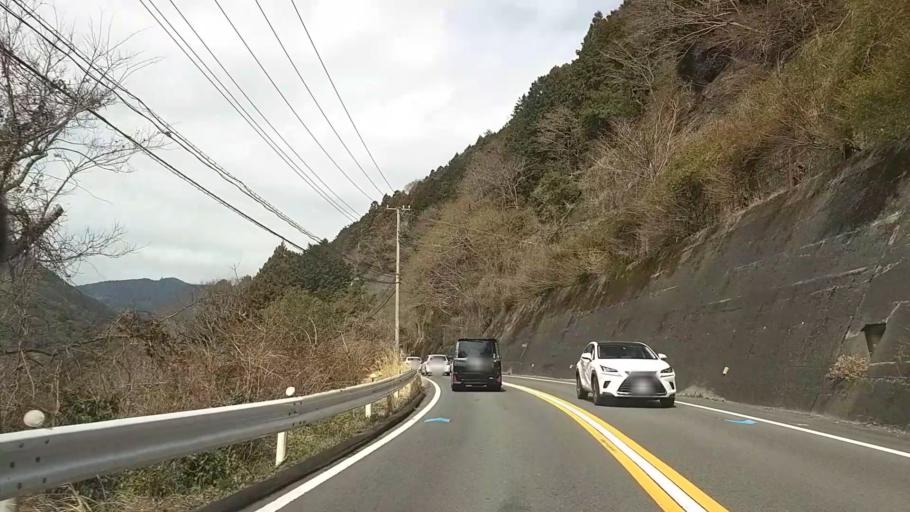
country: JP
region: Shizuoka
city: Shimoda
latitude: 34.7976
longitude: 138.9352
